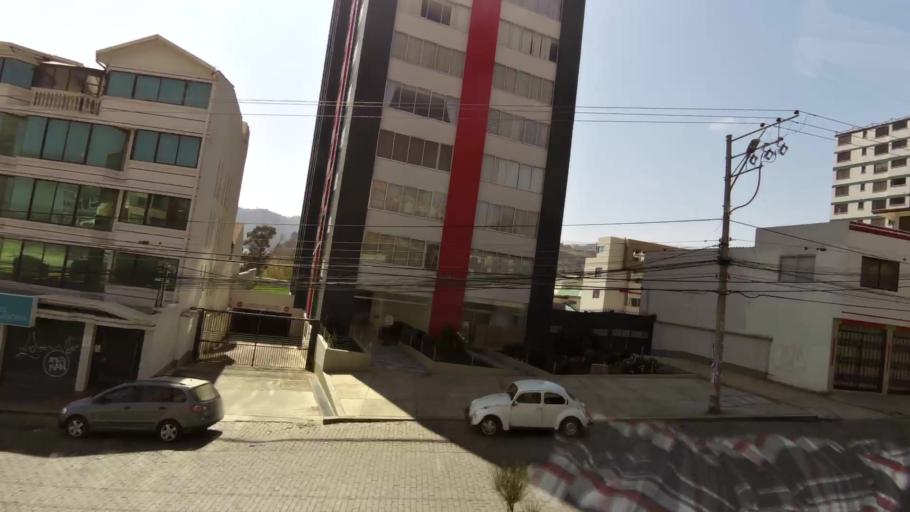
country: BO
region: La Paz
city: La Paz
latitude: -16.5405
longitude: -68.0689
